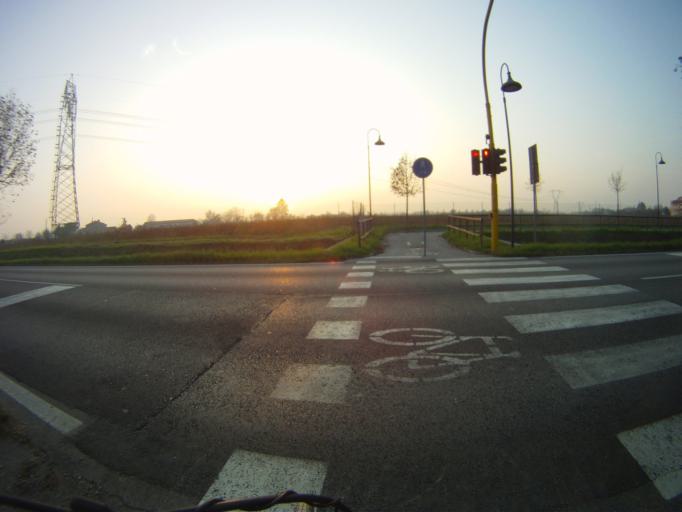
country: IT
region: Veneto
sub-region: Provincia di Padova
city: Albignasego
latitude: 45.3562
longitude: 11.8955
